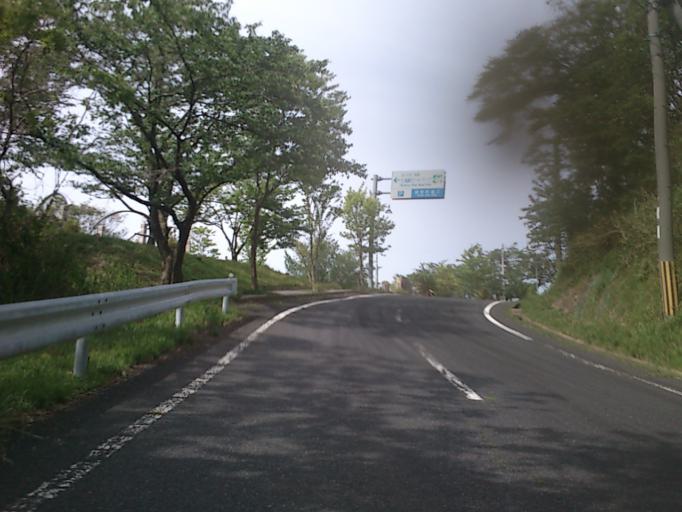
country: JP
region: Hyogo
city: Toyooka
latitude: 35.6810
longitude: 134.9823
